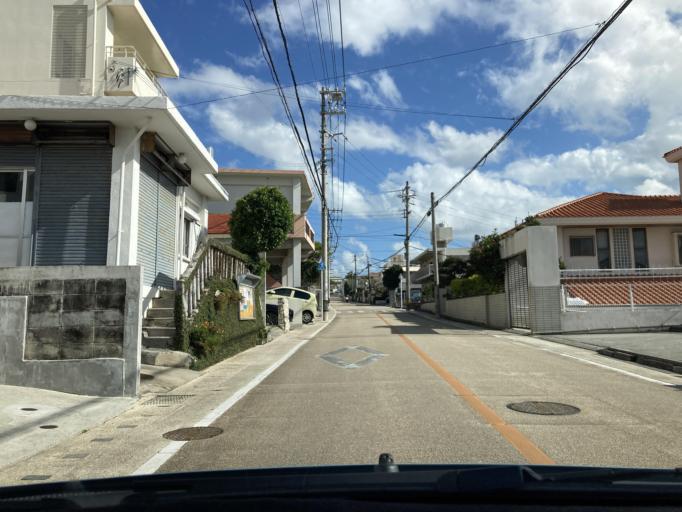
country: JP
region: Okinawa
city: Naha-shi
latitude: 26.2183
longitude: 127.7094
